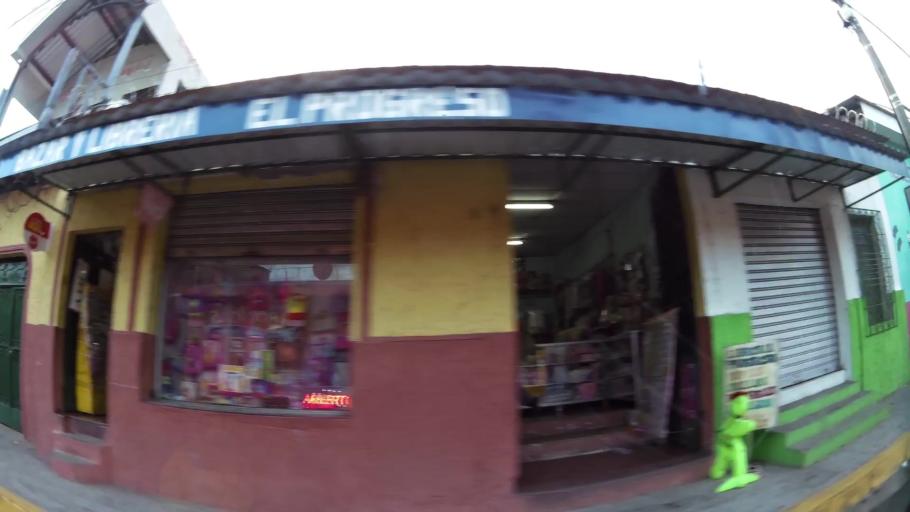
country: SV
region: San Vicente
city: San Vicente
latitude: 13.6428
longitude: -88.7842
